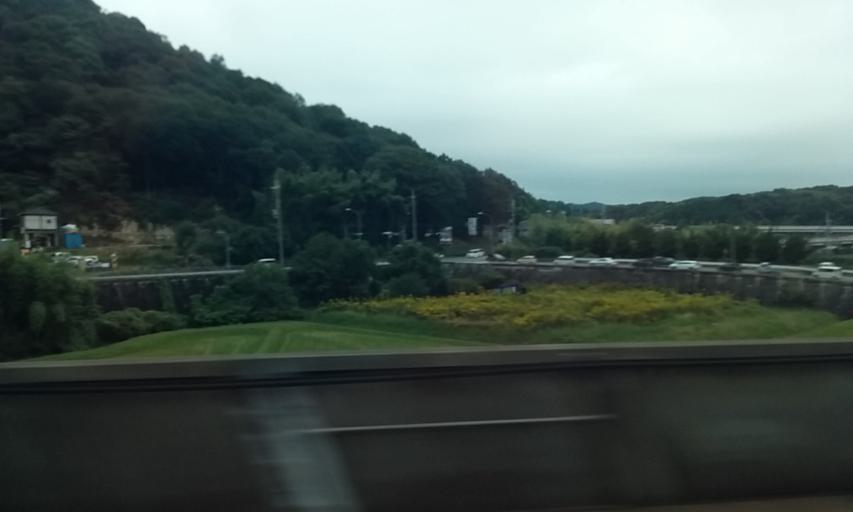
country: JP
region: Hyogo
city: Tatsunocho-tominaga
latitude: 34.8298
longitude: 134.6199
